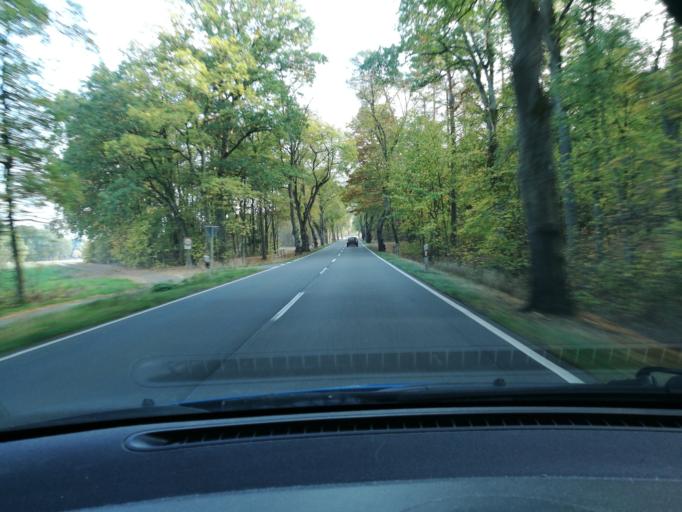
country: DE
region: Lower Saxony
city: Karwitz
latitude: 53.1104
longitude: 11.0175
